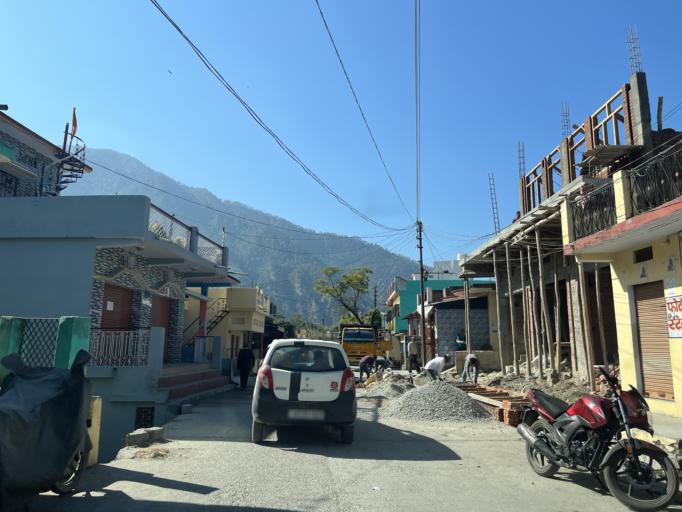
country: IN
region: Uttarakhand
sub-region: Almora
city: Ranikhet
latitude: 29.5553
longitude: 79.3413
